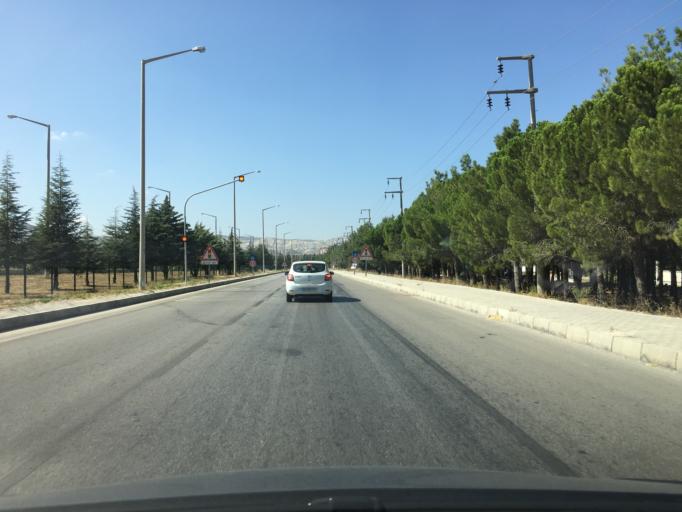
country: TR
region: Burdur
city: Burdur
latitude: 37.7317
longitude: 30.3076
